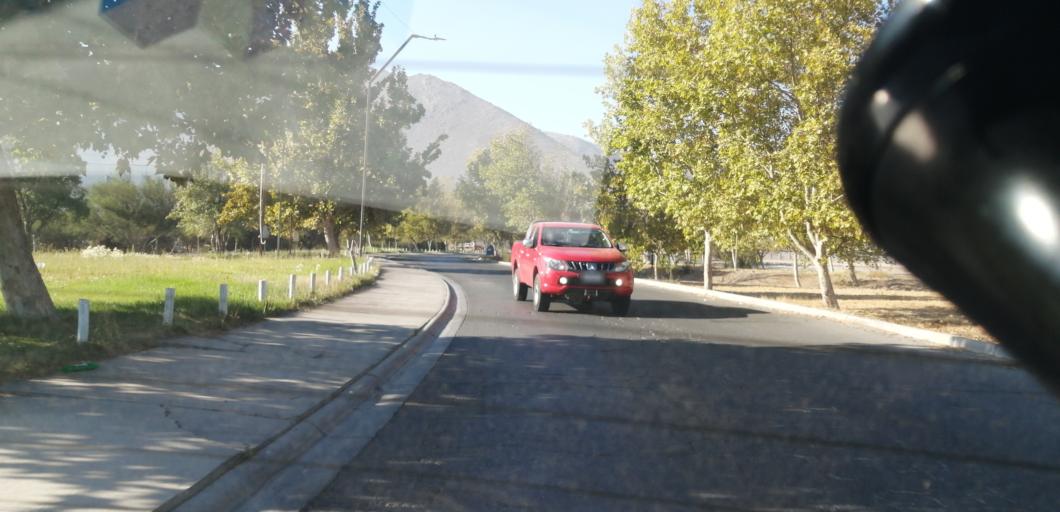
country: CL
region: Santiago Metropolitan
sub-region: Provincia de Santiago
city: Lo Prado
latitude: -33.4438
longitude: -70.8464
